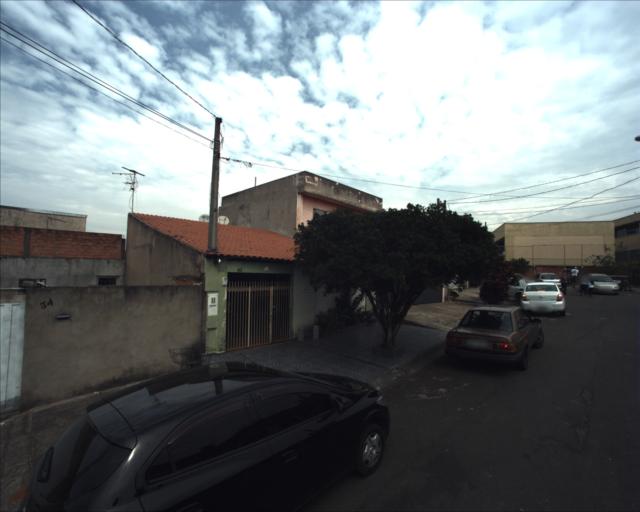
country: BR
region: Sao Paulo
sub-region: Sorocaba
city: Sorocaba
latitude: -23.4990
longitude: -47.5223
